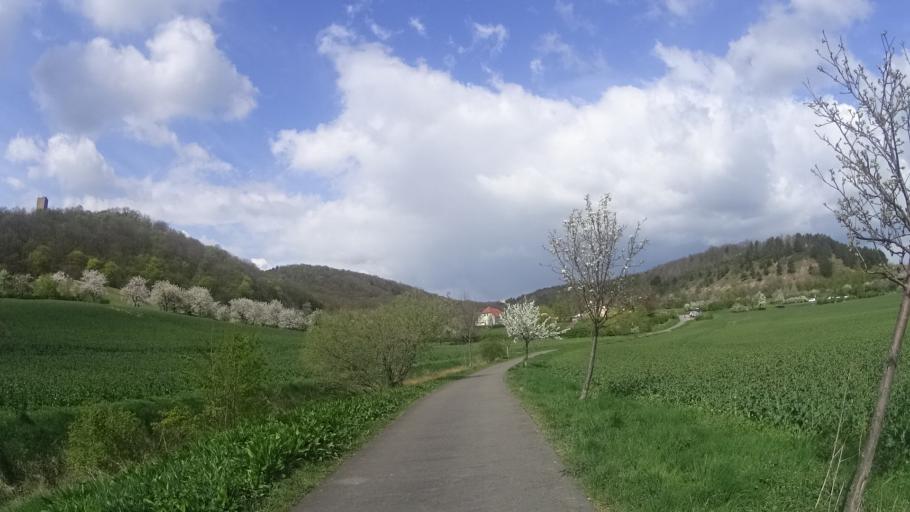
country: DE
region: Thuringia
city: Wandersleben
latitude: 50.8815
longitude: 10.8457
